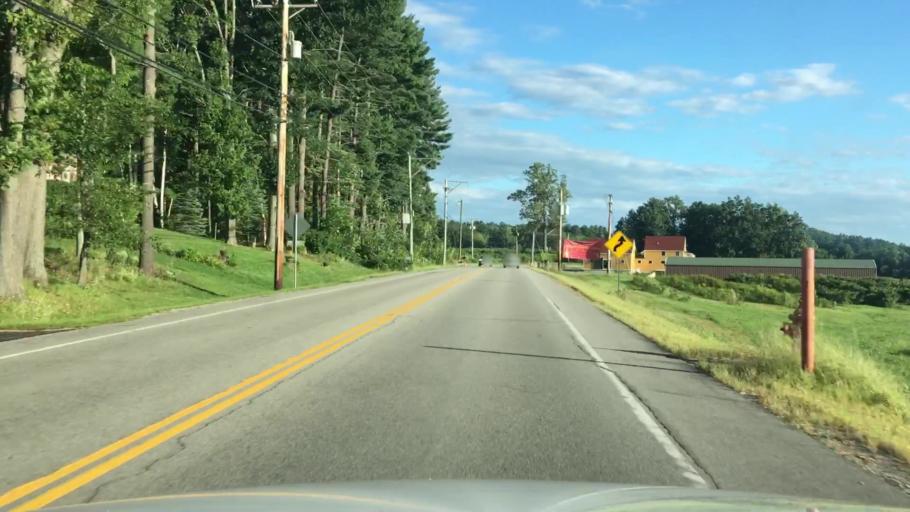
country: US
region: New Hampshire
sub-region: Strafford County
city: Dover
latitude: 43.1638
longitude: -70.8441
